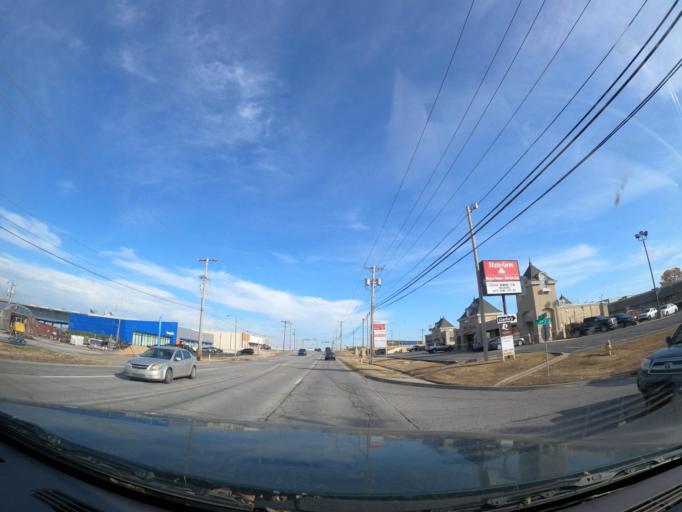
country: US
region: Oklahoma
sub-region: Tulsa County
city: Tulsa
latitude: 36.1044
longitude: -95.8967
